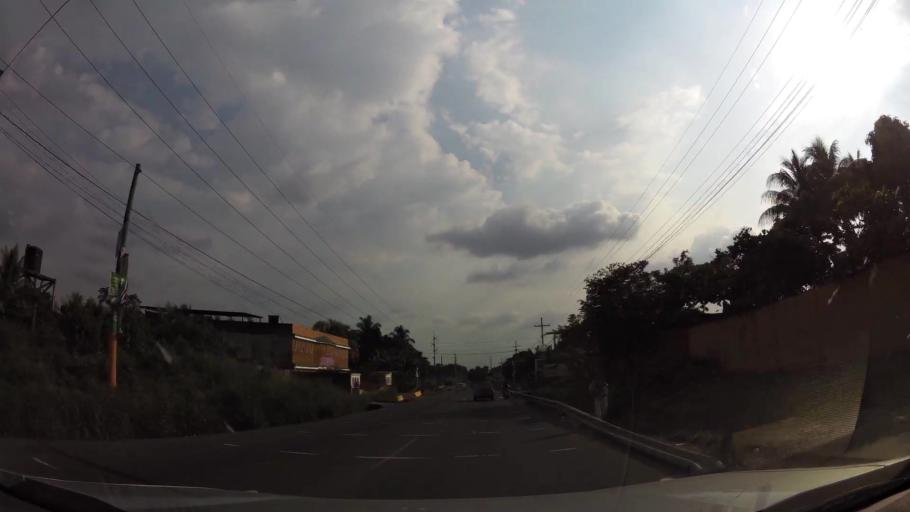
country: GT
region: Escuintla
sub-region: Municipio de Escuintla
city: Escuintla
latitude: 14.3138
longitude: -90.7931
